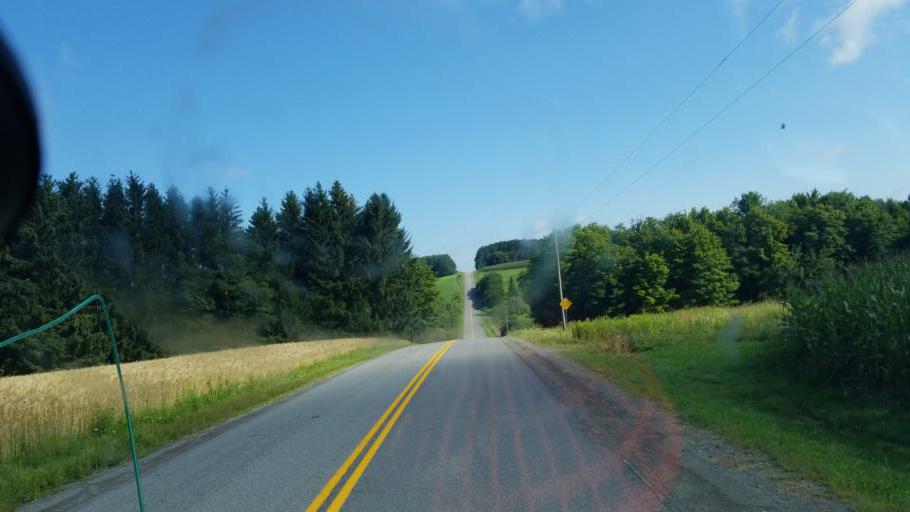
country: US
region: New York
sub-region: Allegany County
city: Andover
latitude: 42.1561
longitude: -77.7135
